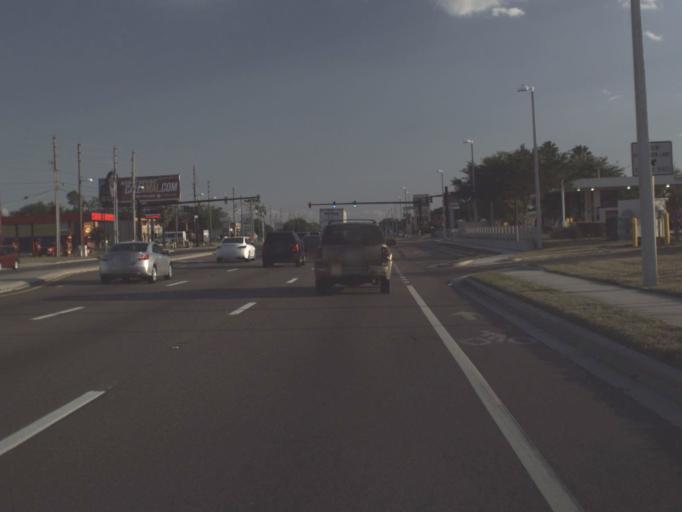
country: US
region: Florida
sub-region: Orange County
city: Southchase
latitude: 28.4044
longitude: -81.4048
